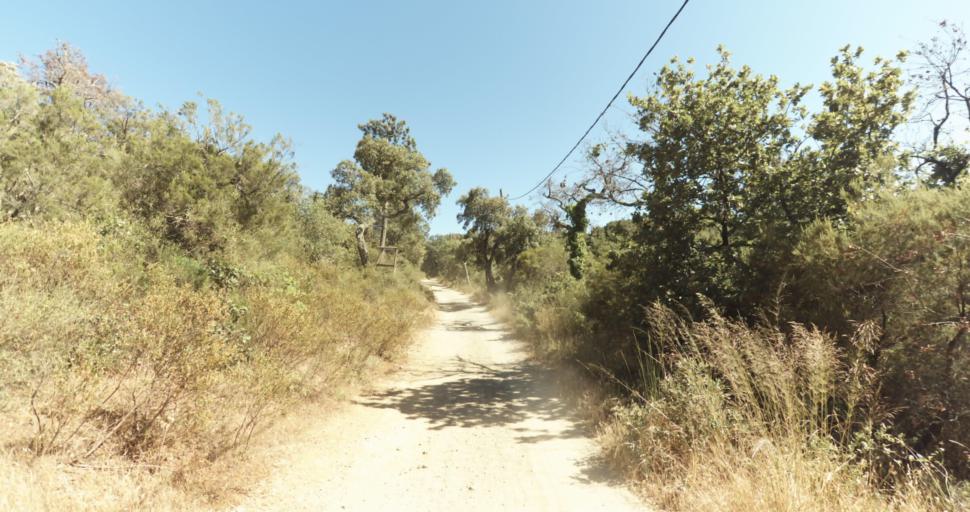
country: FR
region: Provence-Alpes-Cote d'Azur
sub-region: Departement du Var
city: Gassin
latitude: 43.2396
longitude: 6.5843
